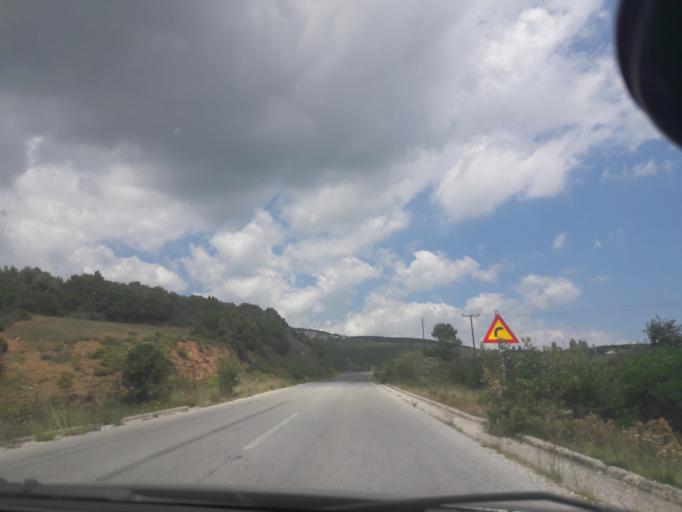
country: GR
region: Central Macedonia
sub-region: Nomos Chalkidikis
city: Polygyros
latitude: 40.3736
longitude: 23.5171
